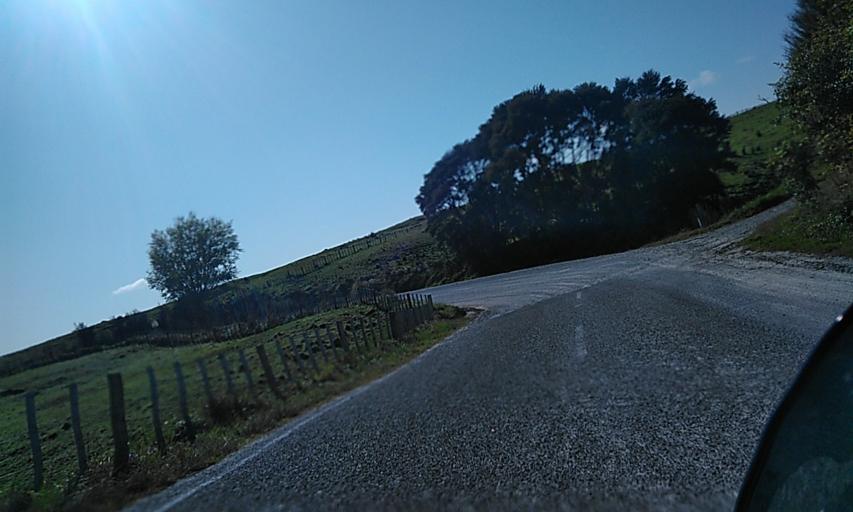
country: NZ
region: Gisborne
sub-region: Gisborne District
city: Gisborne
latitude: -38.4943
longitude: 178.0588
